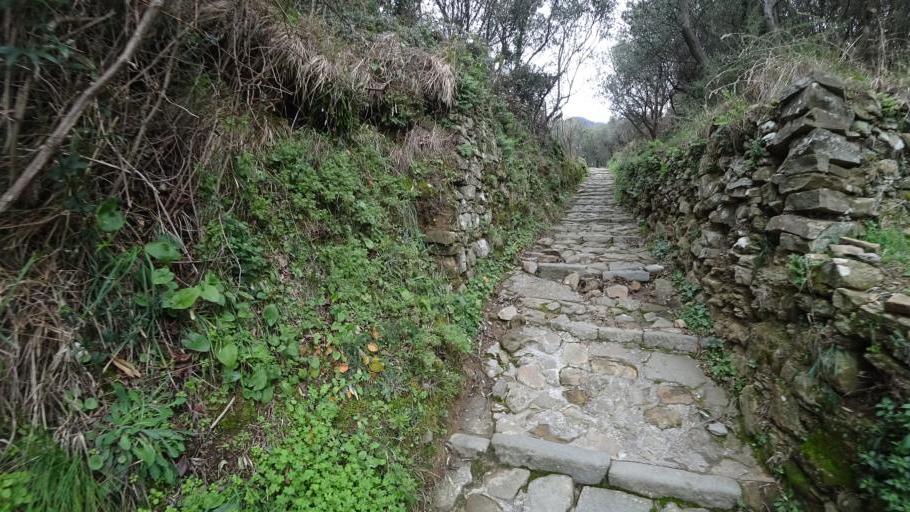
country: IT
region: Liguria
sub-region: Provincia di La Spezia
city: Riomaggiore
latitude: 44.1134
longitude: 9.7302
